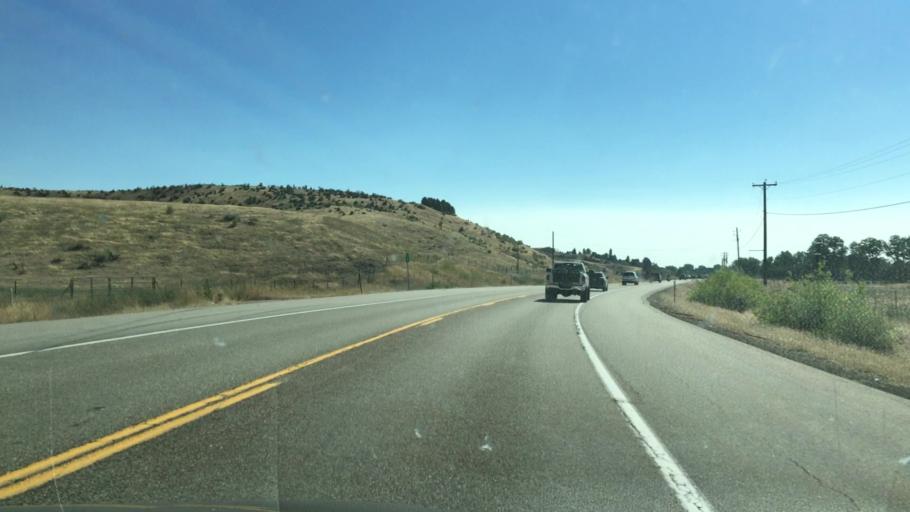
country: US
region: Idaho
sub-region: Ada County
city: Eagle
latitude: 43.7282
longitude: -116.3056
